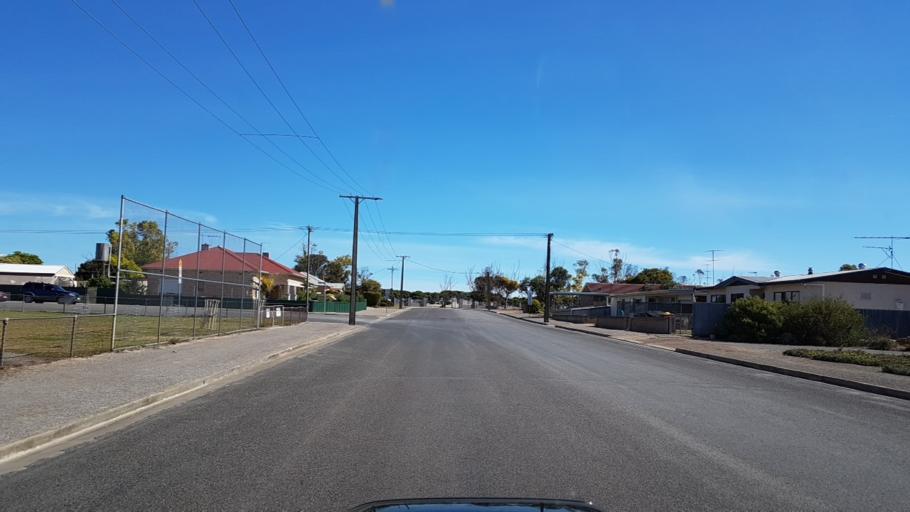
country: AU
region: South Australia
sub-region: Yorke Peninsula
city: Honiton
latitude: -34.9906
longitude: 137.3985
